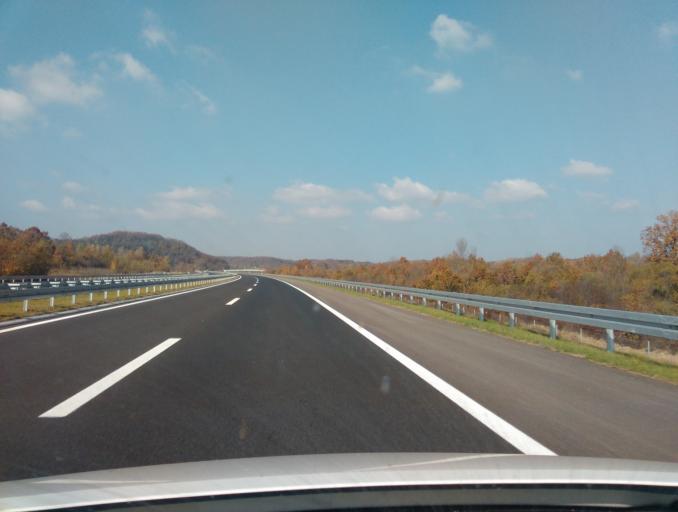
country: BA
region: Republika Srpska
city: Prnjavor
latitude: 44.8835
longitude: 17.6185
